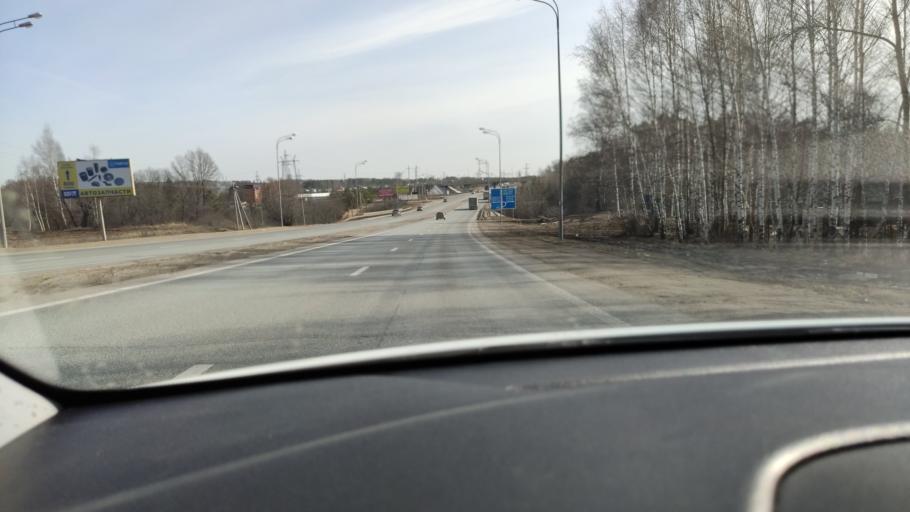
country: RU
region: Tatarstan
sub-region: Gorod Kazan'
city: Kazan
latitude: 55.9176
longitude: 49.1357
